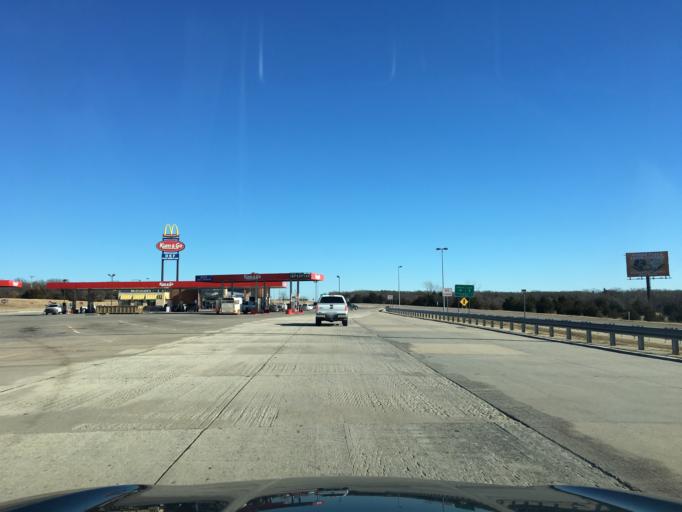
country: US
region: Oklahoma
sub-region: Pawnee County
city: Pawnee
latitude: 36.2245
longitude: -96.7975
